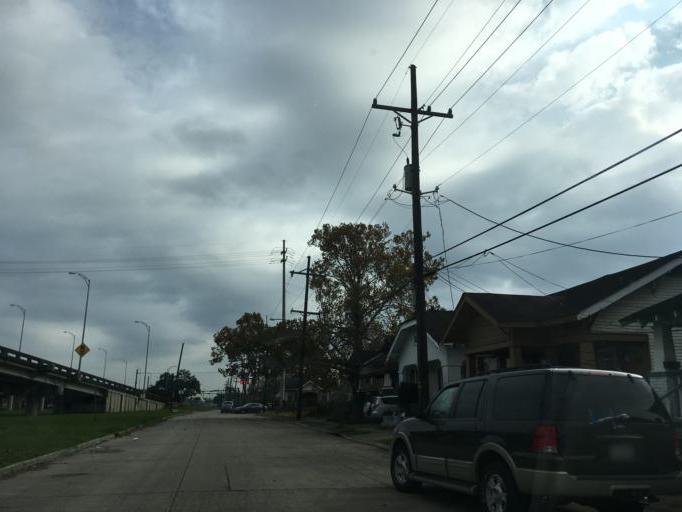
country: US
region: Louisiana
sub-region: Orleans Parish
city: New Orleans
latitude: 29.9907
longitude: -90.0608
